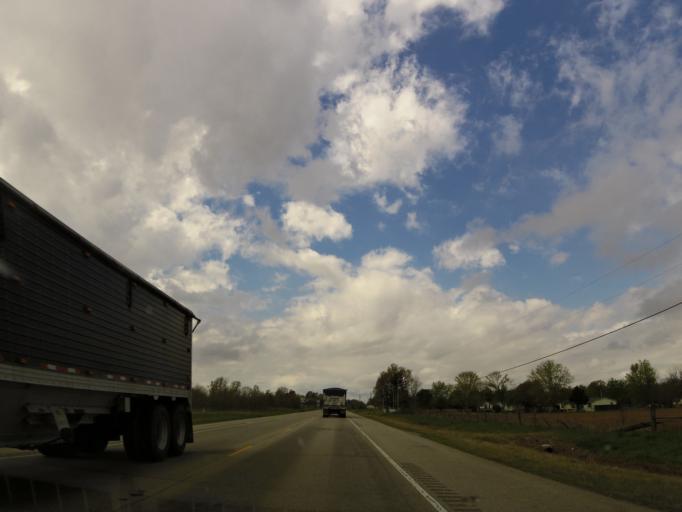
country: US
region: Arkansas
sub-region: Clay County
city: Corning
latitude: 36.4632
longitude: -90.5737
